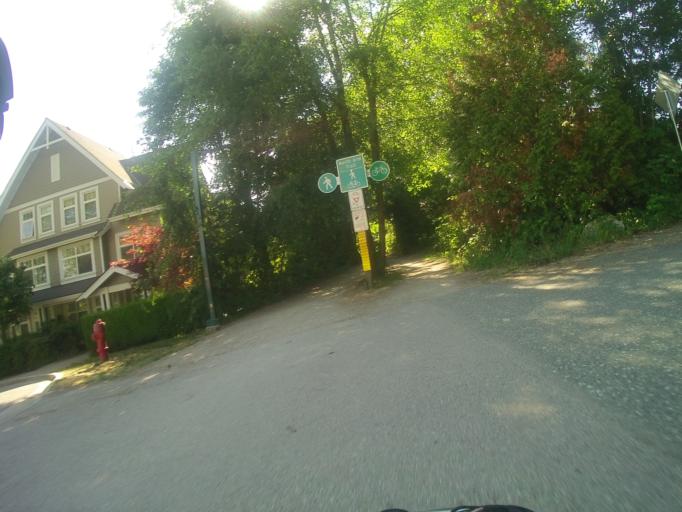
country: CA
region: British Columbia
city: Vancouver
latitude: 49.2177
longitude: -123.1110
